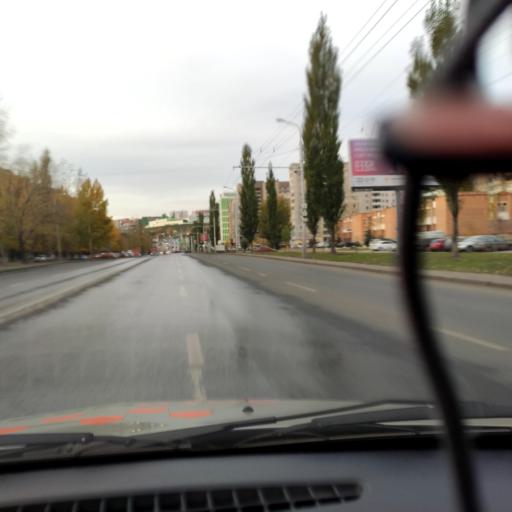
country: RU
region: Bashkortostan
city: Ufa
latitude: 54.7683
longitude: 56.0543
